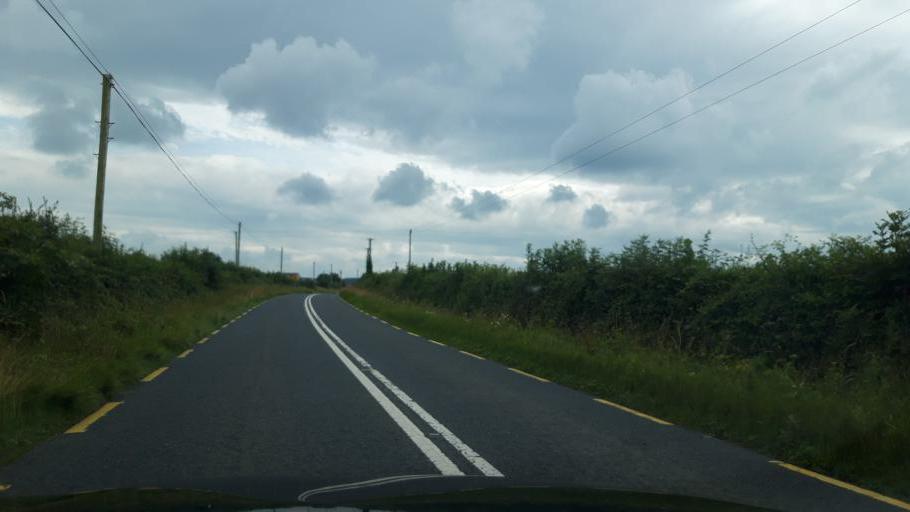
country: IE
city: Ballylinan
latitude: 52.9253
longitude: -7.0615
